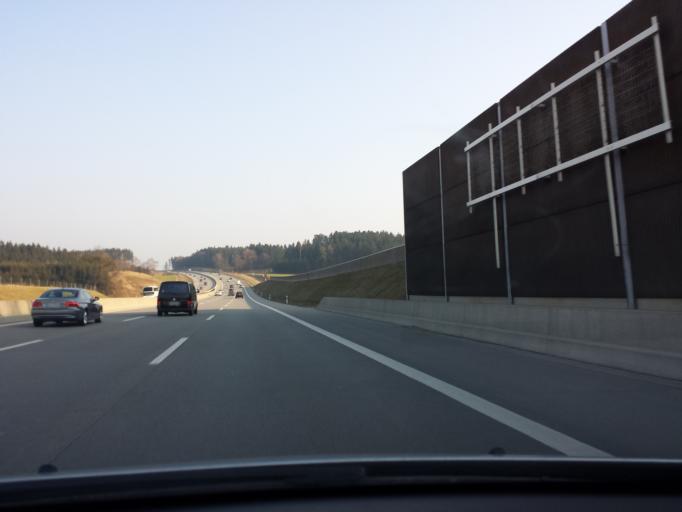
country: DE
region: Bavaria
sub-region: Swabia
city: Eurasburg
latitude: 48.3737
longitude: 11.0967
